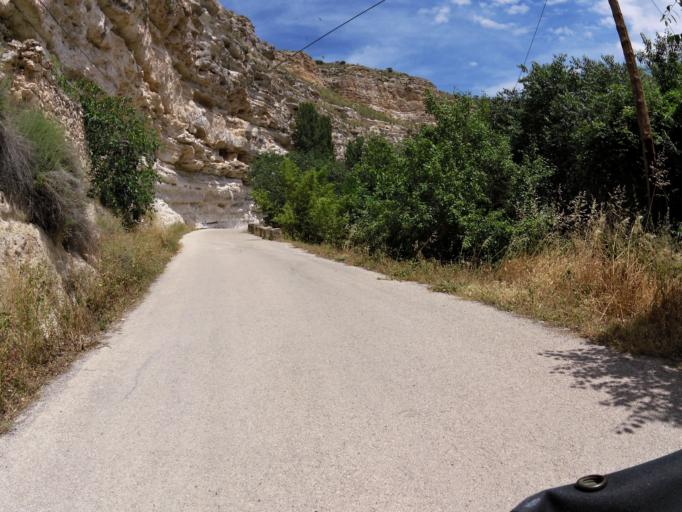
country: ES
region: Castille-La Mancha
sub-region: Provincia de Albacete
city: Valdeganga
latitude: 39.1628
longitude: -1.6073
